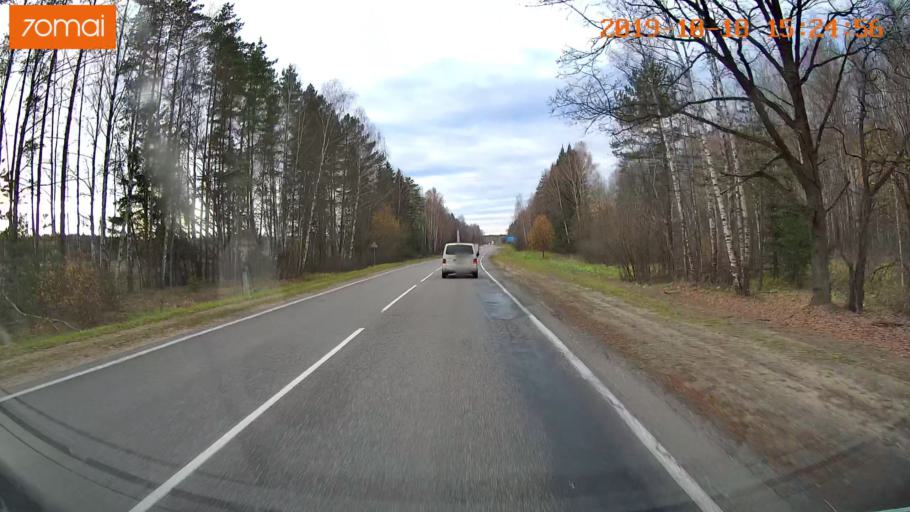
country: RU
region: Vladimir
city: Anopino
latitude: 55.7380
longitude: 40.7150
